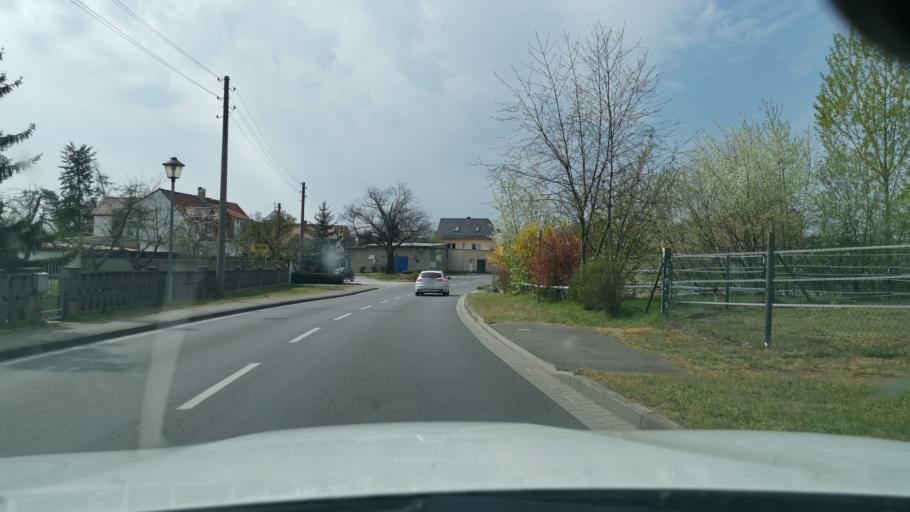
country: DE
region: Saxony
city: Lobnitz
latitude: 51.5569
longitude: 12.4588
